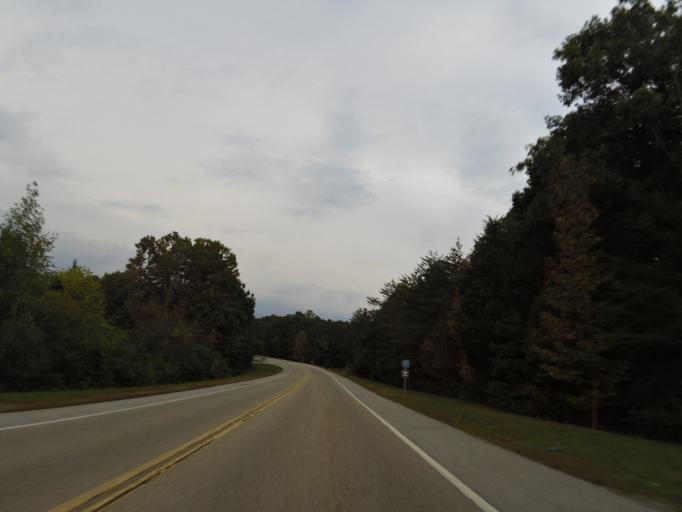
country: US
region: Tennessee
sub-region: Loudon County
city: Loudon
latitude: 35.6815
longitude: -84.2643
